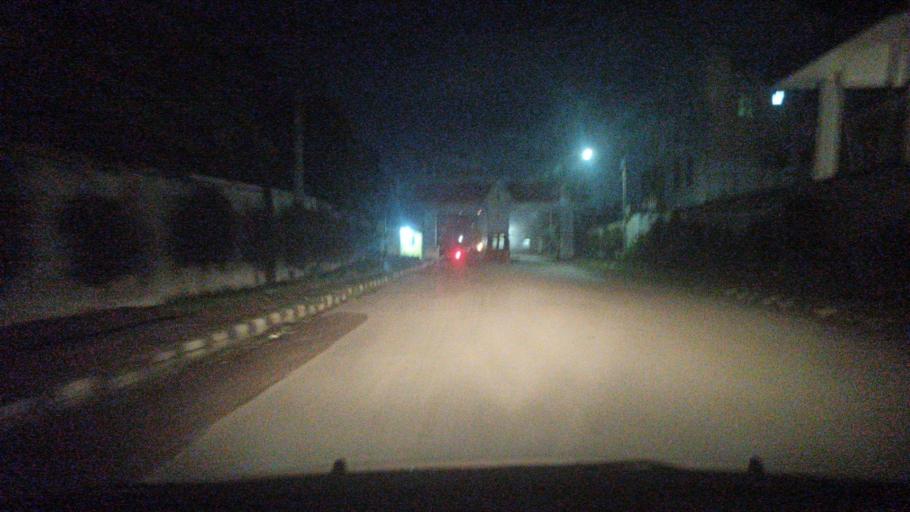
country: ID
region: South Sumatra
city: Plaju
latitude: -3.0072
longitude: 104.7212
